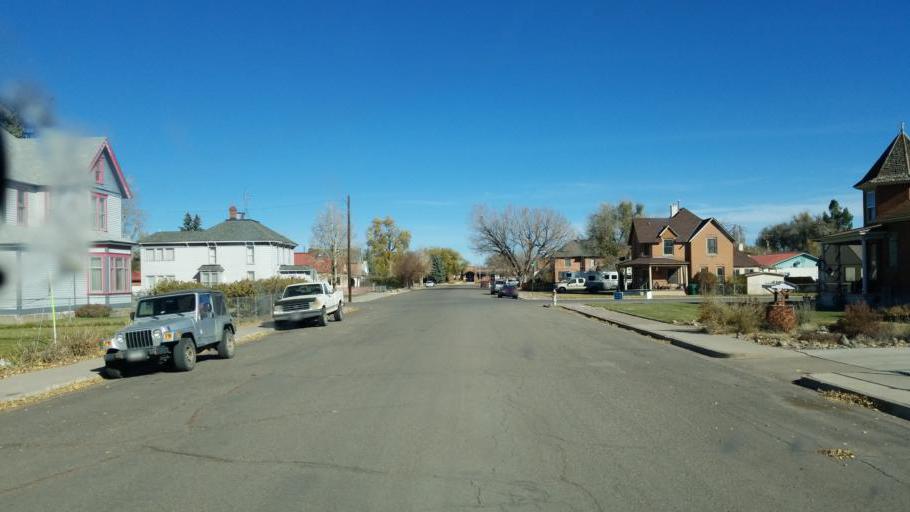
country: US
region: Colorado
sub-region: Rio Grande County
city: Monte Vista
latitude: 37.5774
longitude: -106.1509
